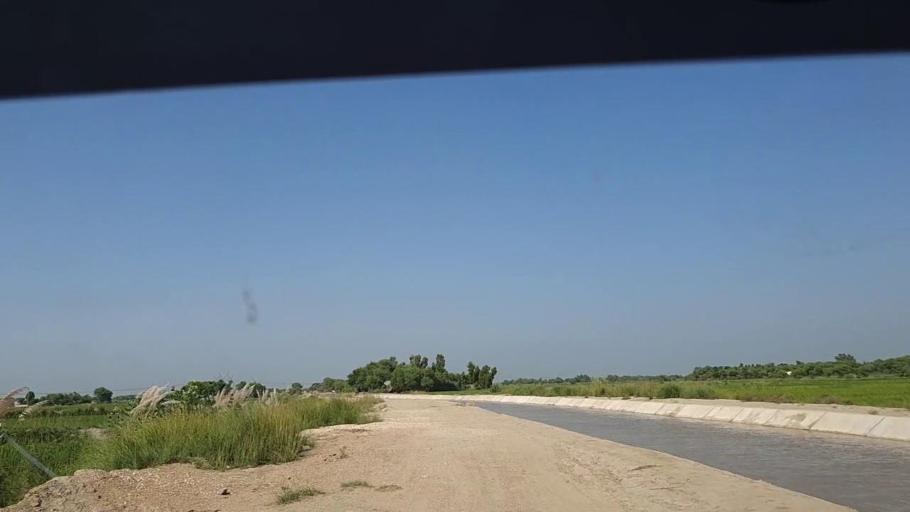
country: PK
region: Sindh
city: Ghauspur
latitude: 28.1622
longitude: 69.0946
